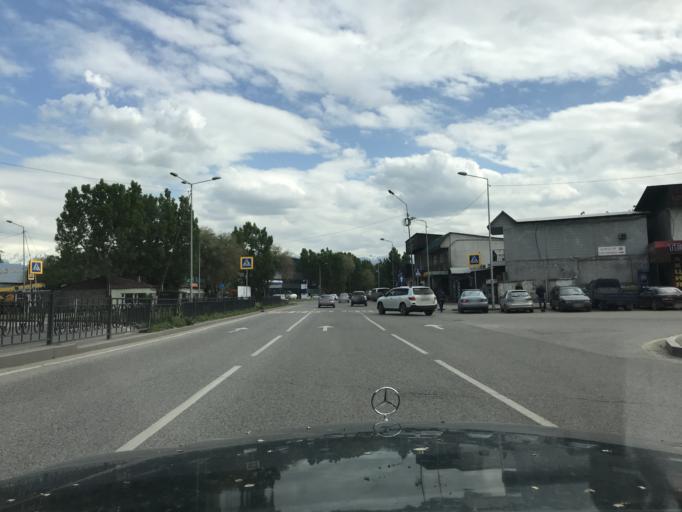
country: KZ
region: Almaty Qalasy
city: Almaty
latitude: 43.3018
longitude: 76.8971
